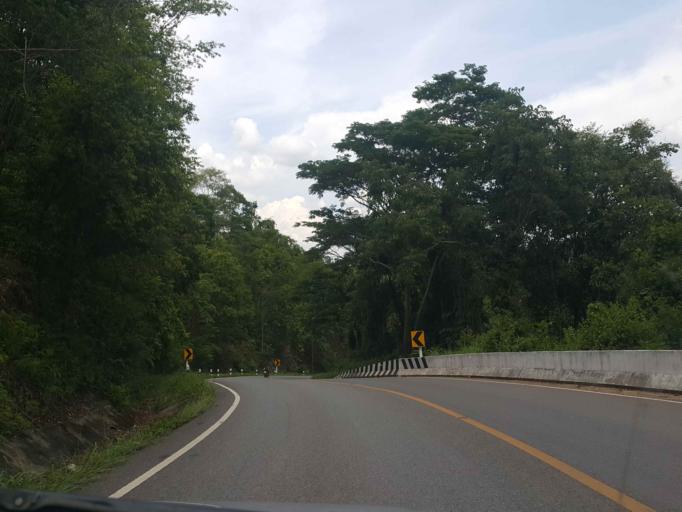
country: TH
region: Nan
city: Nan
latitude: 18.8650
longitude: 100.6320
